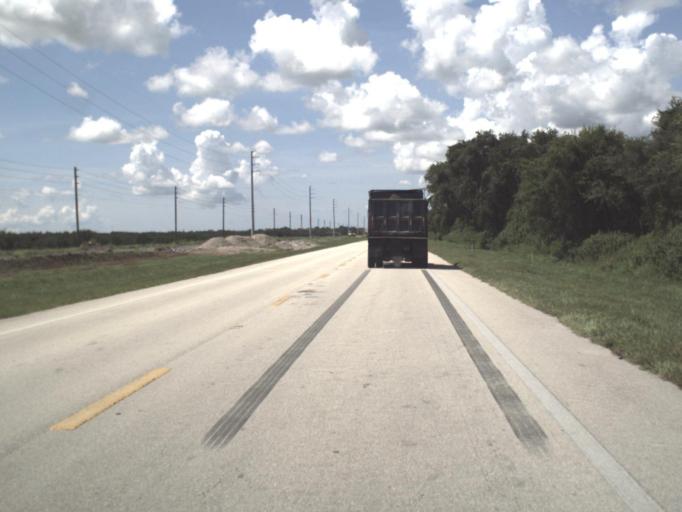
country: US
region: Florida
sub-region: DeSoto County
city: Nocatee
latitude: 27.1176
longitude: -81.9191
